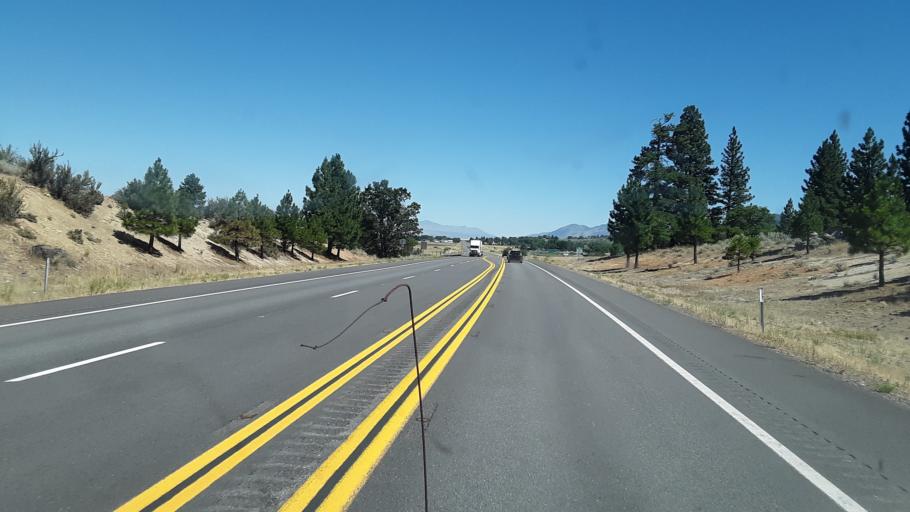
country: US
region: California
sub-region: Lassen County
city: Janesville
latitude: 40.3049
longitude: -120.5272
